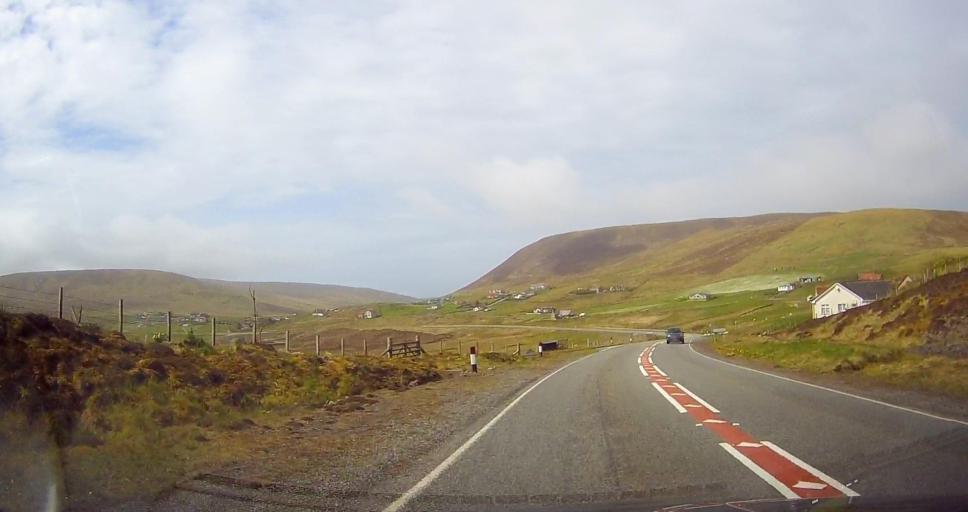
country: GB
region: Scotland
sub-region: Shetland Islands
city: Lerwick
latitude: 60.1044
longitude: -1.2228
